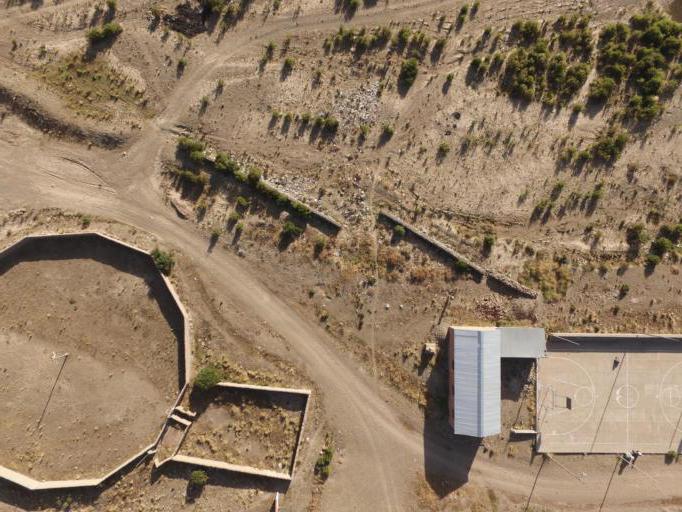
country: BO
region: Oruro
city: Challapata
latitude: -18.6918
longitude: -66.7583
